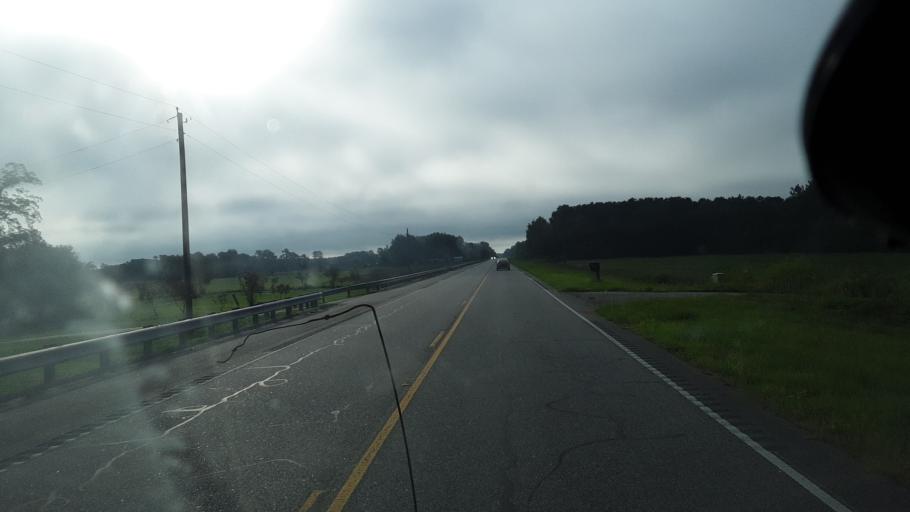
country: US
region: South Carolina
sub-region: Horry County
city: Red Hill
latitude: 33.8477
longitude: -79.2888
